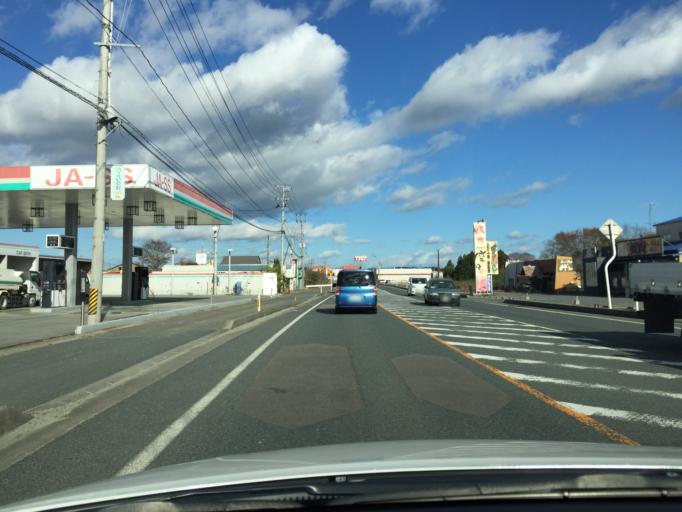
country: JP
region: Fukushima
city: Namie
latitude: 37.4852
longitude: 141.0054
